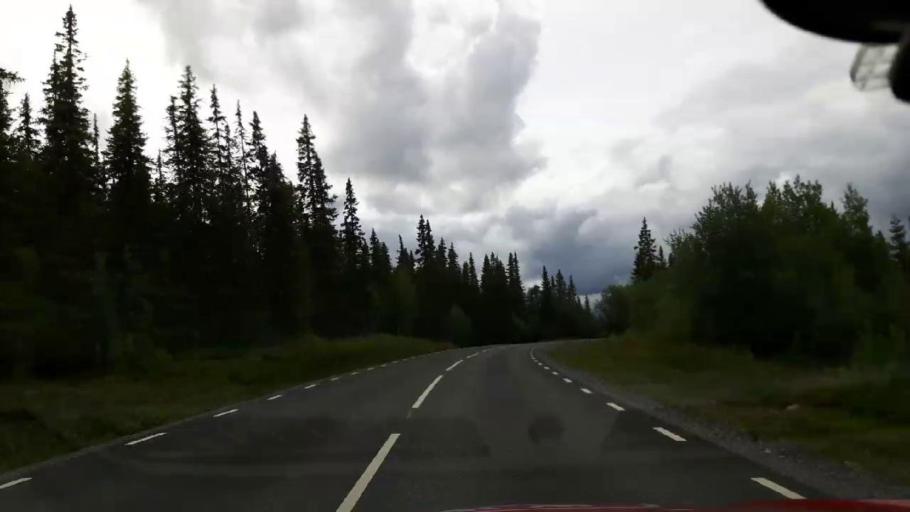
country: NO
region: Nord-Trondelag
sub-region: Lierne
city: Sandvika
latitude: 64.5966
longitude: 14.1188
